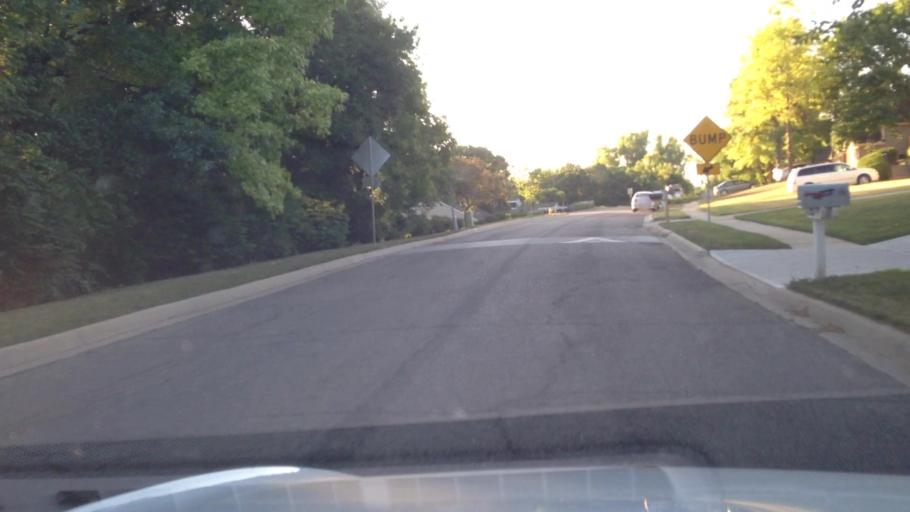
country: US
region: Kansas
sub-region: Douglas County
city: Lawrence
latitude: 38.9446
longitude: -95.2891
